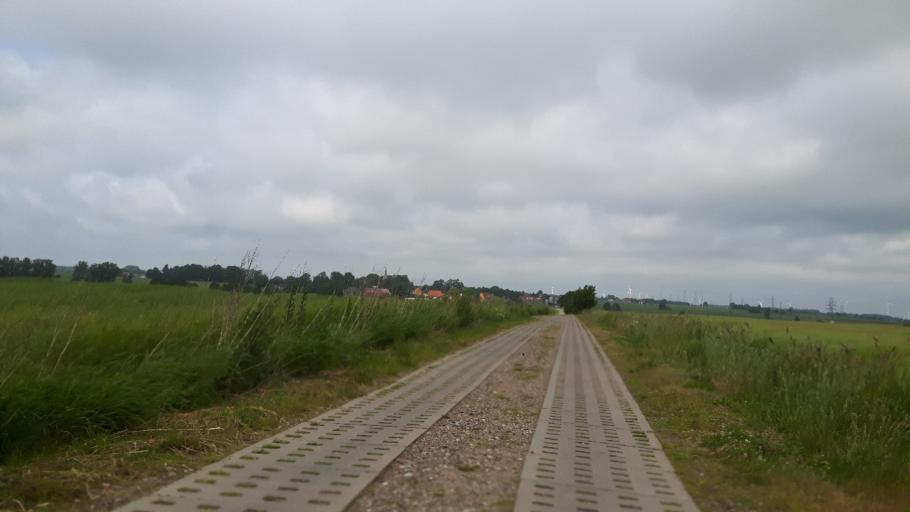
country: PL
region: West Pomeranian Voivodeship
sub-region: Powiat koszalinski
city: Sianow
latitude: 54.2885
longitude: 16.2633
